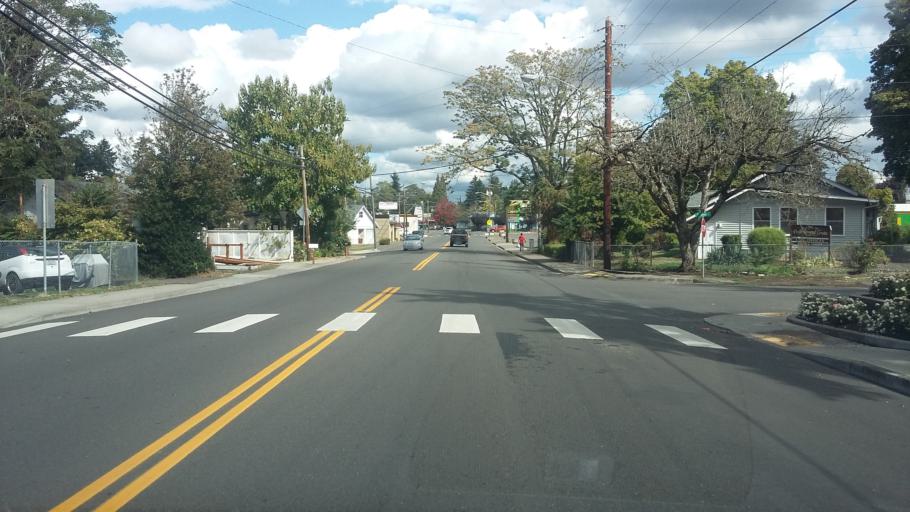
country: US
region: Washington
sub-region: Clark County
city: Vancouver
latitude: 45.6408
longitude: -122.6504
